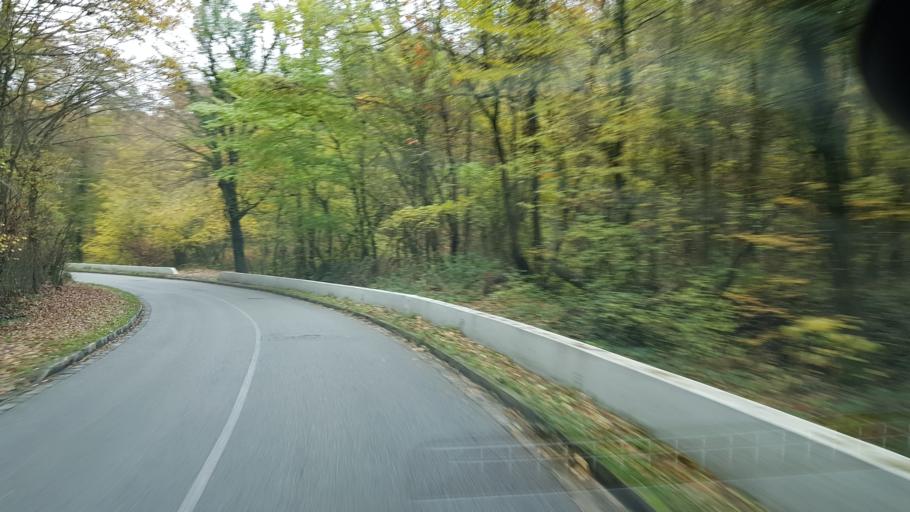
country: FR
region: Ile-de-France
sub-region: Departement des Yvelines
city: Chevreuse
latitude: 48.7130
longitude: 2.0219
